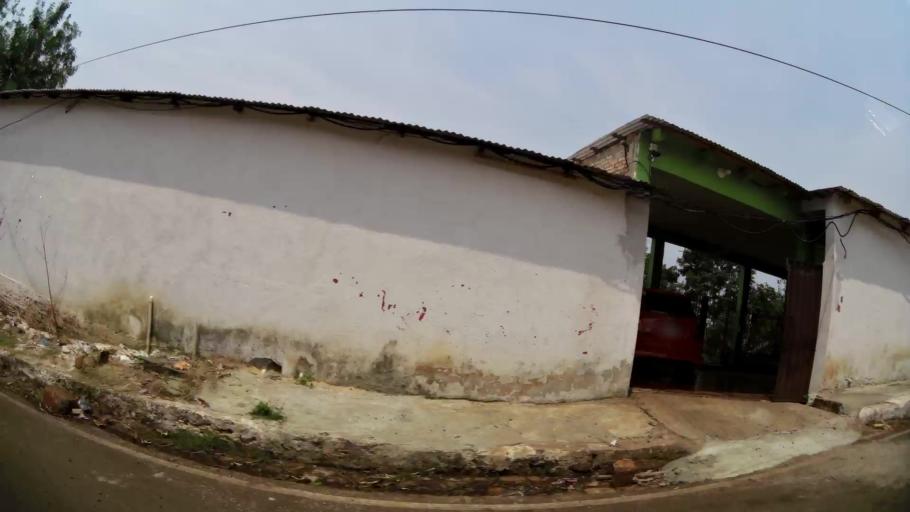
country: AR
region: Misiones
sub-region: Departamento de Iguazu
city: Puerto Iguazu
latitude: -25.5945
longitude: -54.5974
